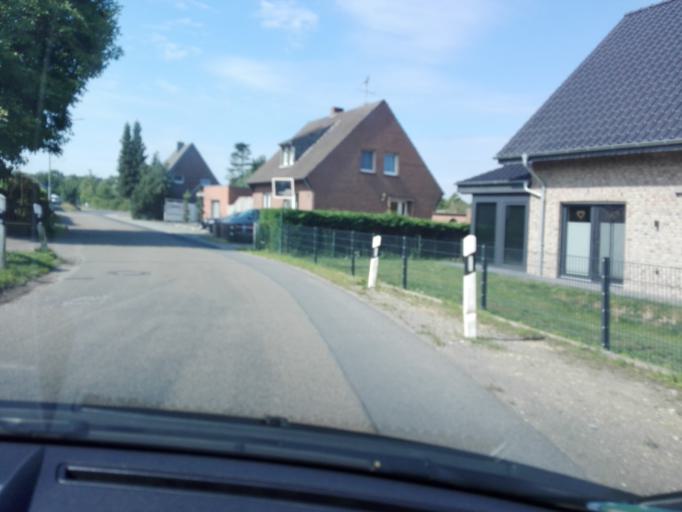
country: DE
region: North Rhine-Westphalia
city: Geldern
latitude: 51.5192
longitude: 6.3511
